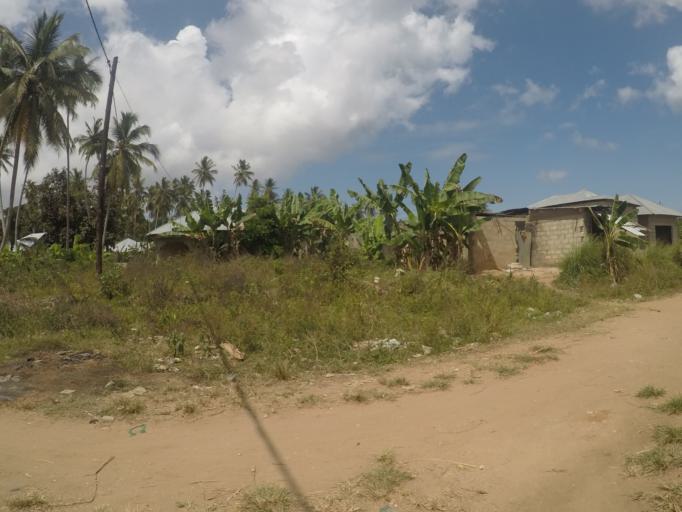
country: TZ
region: Zanzibar Urban/West
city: Zanzibar
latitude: -6.2013
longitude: 39.2380
